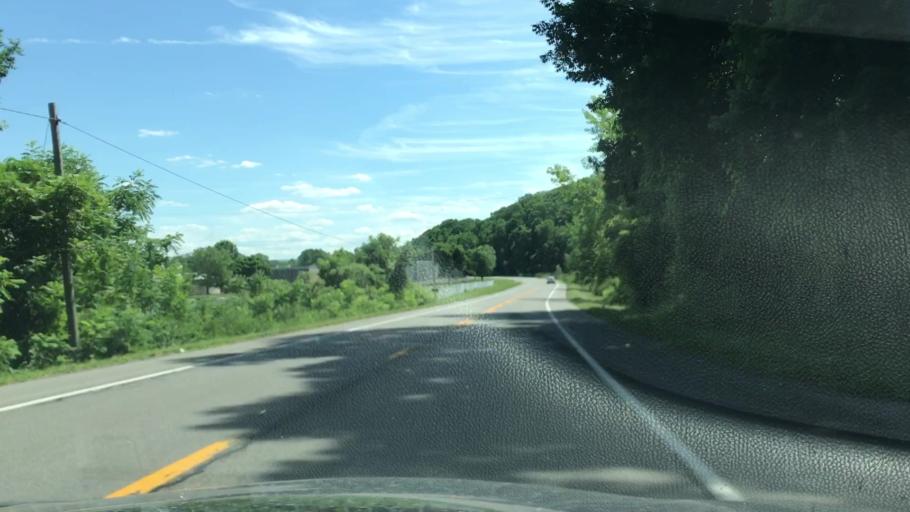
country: US
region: New York
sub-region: Livingston County
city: Mount Morris
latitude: 42.7483
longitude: -77.8832
